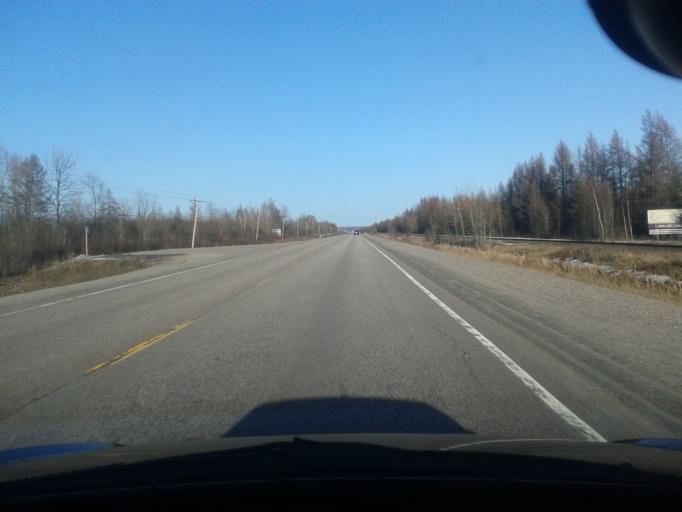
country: CA
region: Ontario
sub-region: Nipissing District
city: North Bay
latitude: 46.3676
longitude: -79.8069
